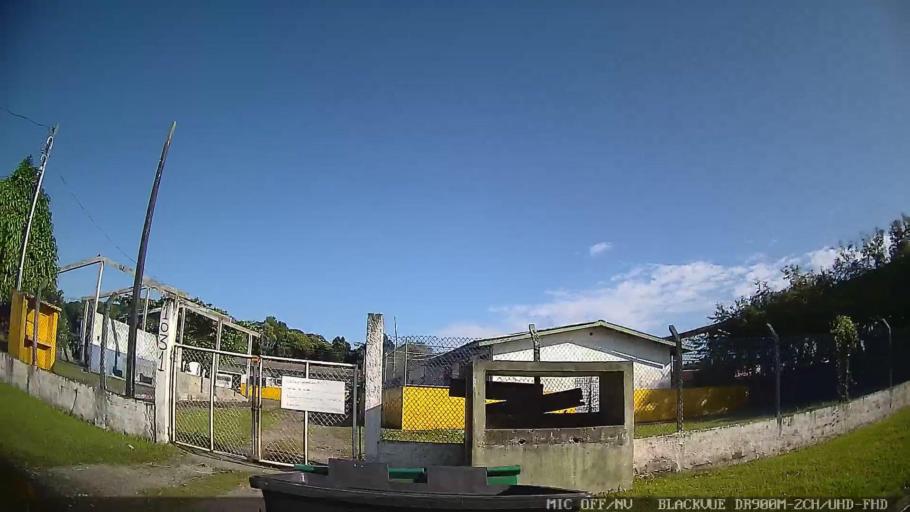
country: BR
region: Sao Paulo
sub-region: Peruibe
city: Peruibe
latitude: -24.2686
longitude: -46.9439
